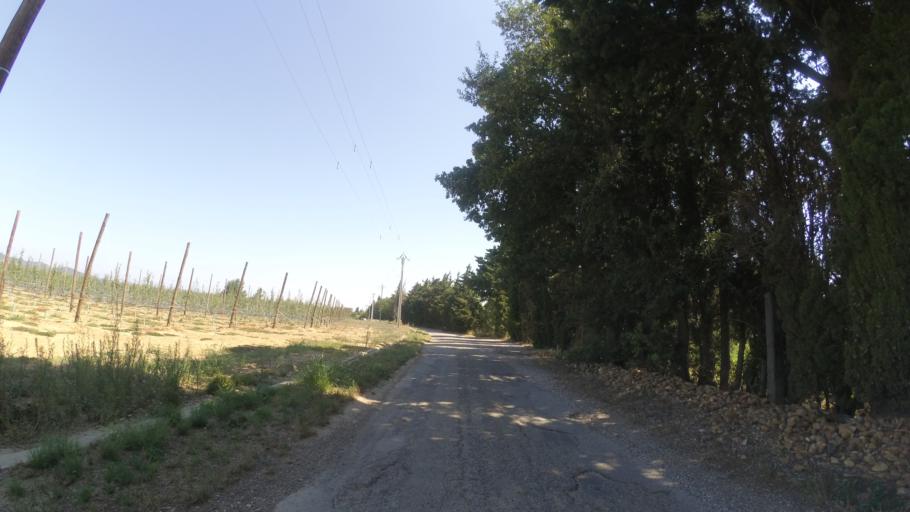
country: FR
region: Languedoc-Roussillon
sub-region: Departement des Pyrenees-Orientales
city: Corneilla-la-Riviere
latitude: 42.6705
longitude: 2.7311
